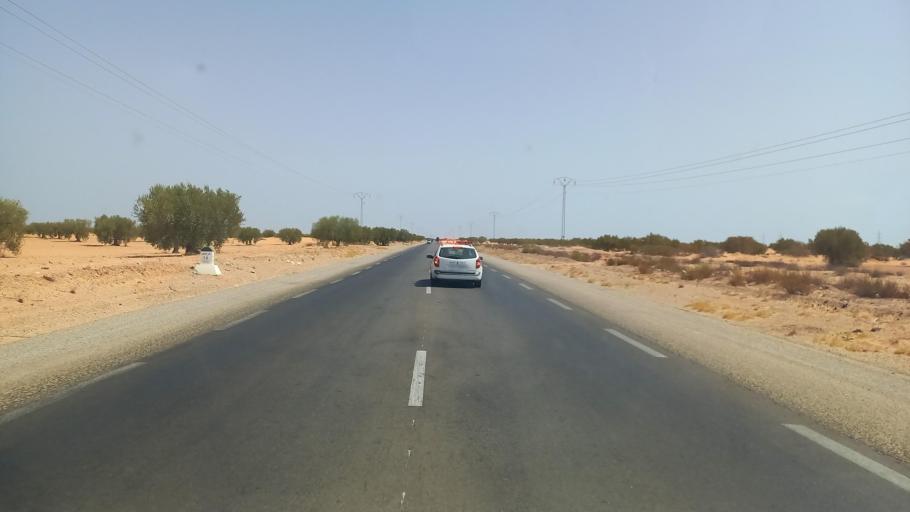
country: TN
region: Madanin
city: Zarzis
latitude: 33.4176
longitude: 10.8743
